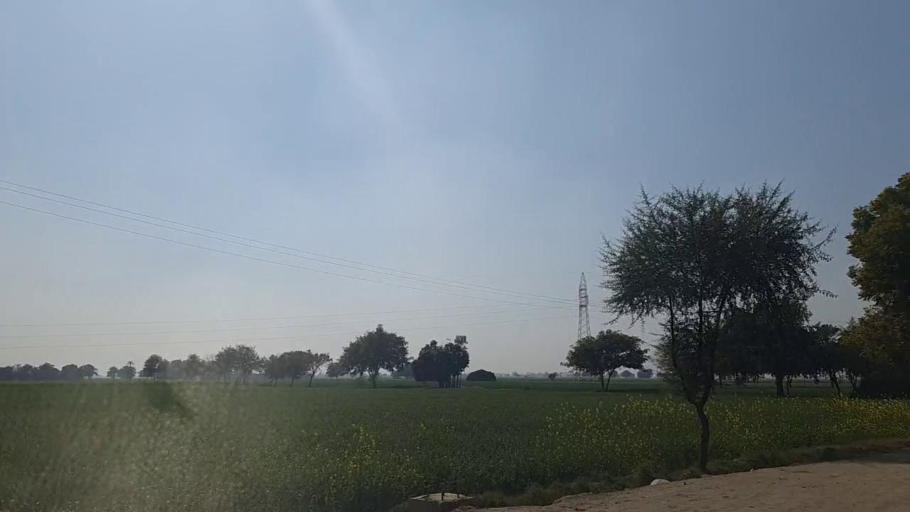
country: PK
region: Sindh
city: Shahpur Chakar
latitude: 26.1906
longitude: 68.5417
